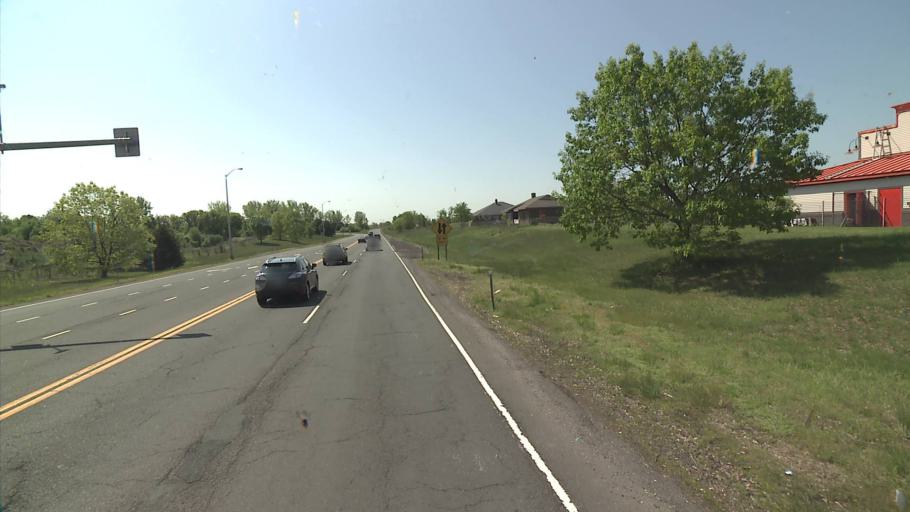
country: US
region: Connecticut
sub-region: Hartford County
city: Manchester
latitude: 41.8048
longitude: -72.5583
